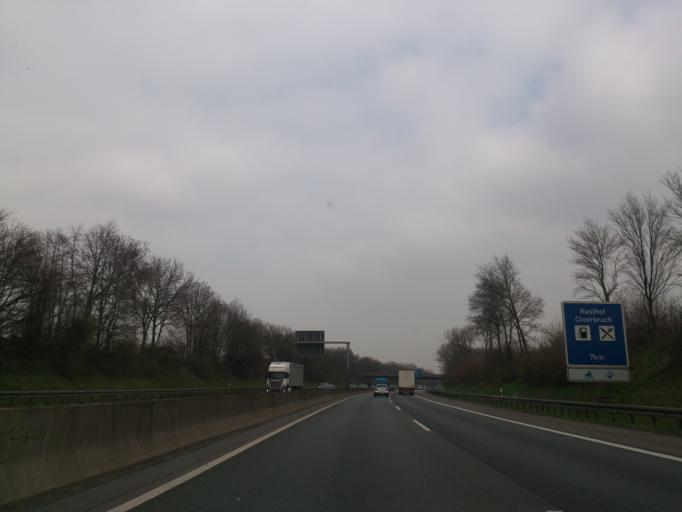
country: DE
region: North Rhine-Westphalia
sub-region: Regierungsbezirk Dusseldorf
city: Viersen
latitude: 51.2218
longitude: 6.4110
